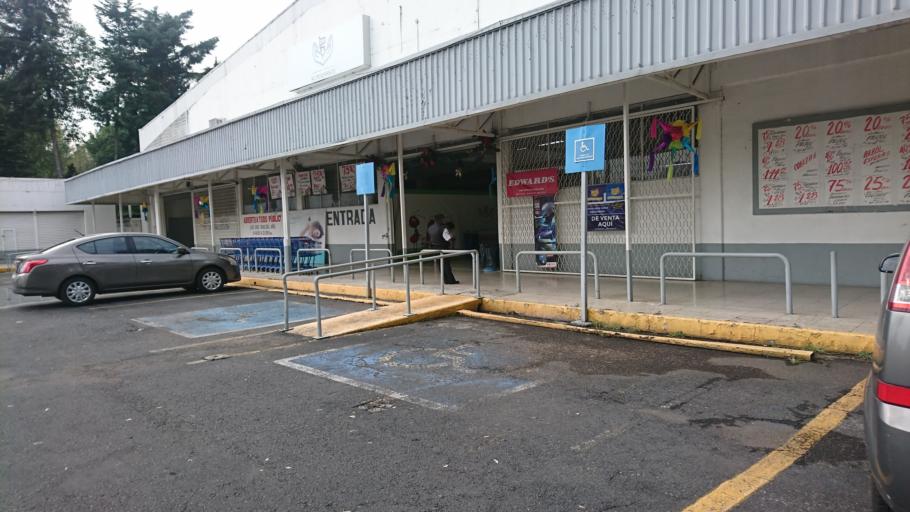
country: MX
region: Mexico City
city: Iztapalapa
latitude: 19.3286
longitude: -99.1084
